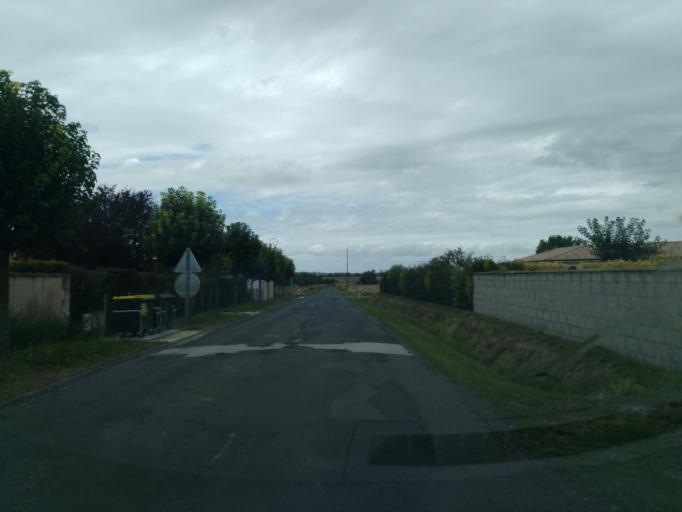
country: FR
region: Poitou-Charentes
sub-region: Departement de la Charente-Maritime
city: Pons
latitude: 45.6006
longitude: -0.5144
